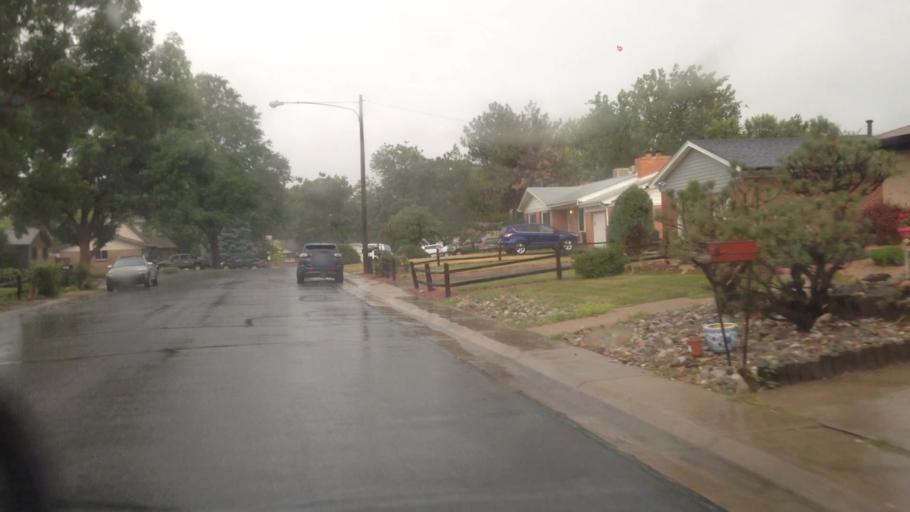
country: US
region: Colorado
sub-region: Jefferson County
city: Lakewood
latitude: 39.7244
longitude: -105.0716
